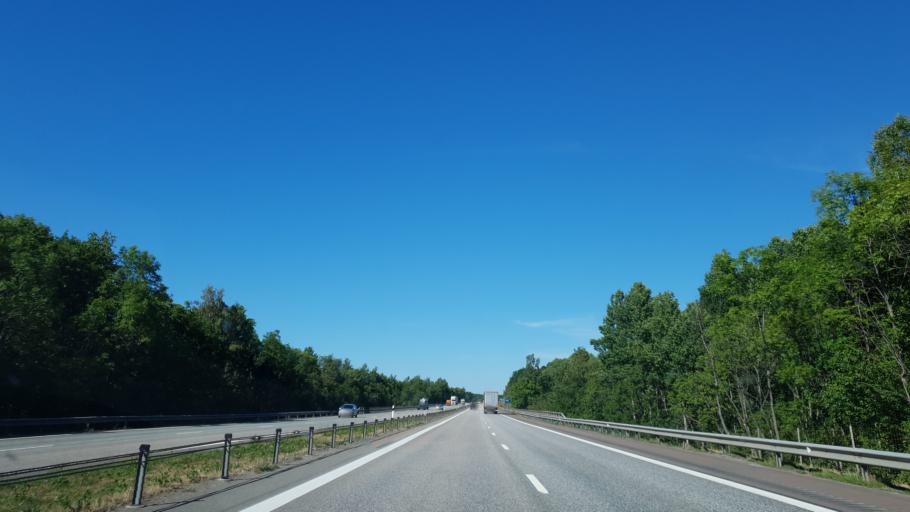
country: SE
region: Joenkoeping
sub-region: Jonkopings Kommun
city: Asa
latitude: 58.1256
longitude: 14.5647
